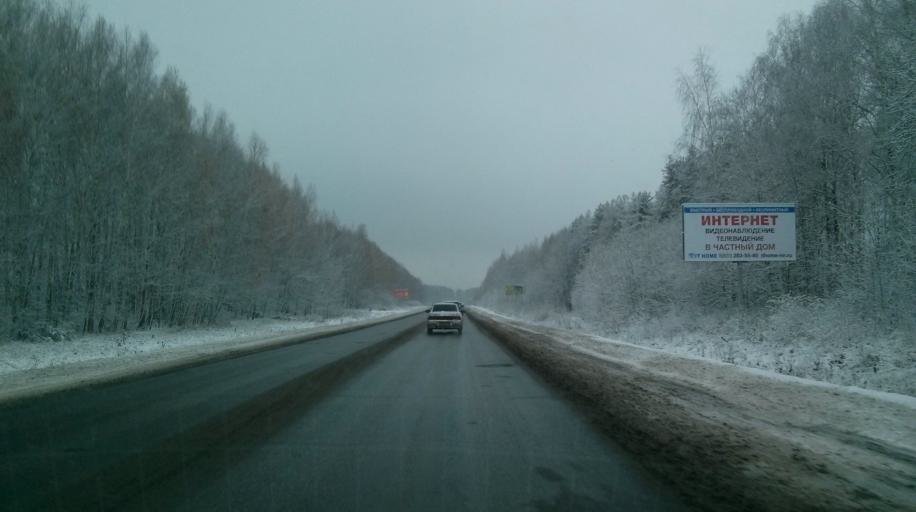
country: RU
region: Nizjnij Novgorod
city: Burevestnik
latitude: 56.1538
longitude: 43.7004
